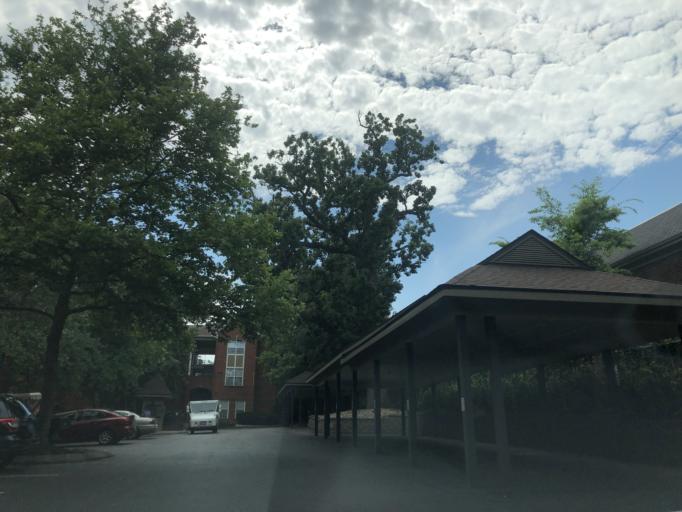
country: US
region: Tennessee
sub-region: Davidson County
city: Nashville
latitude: 36.1317
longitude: -86.8211
